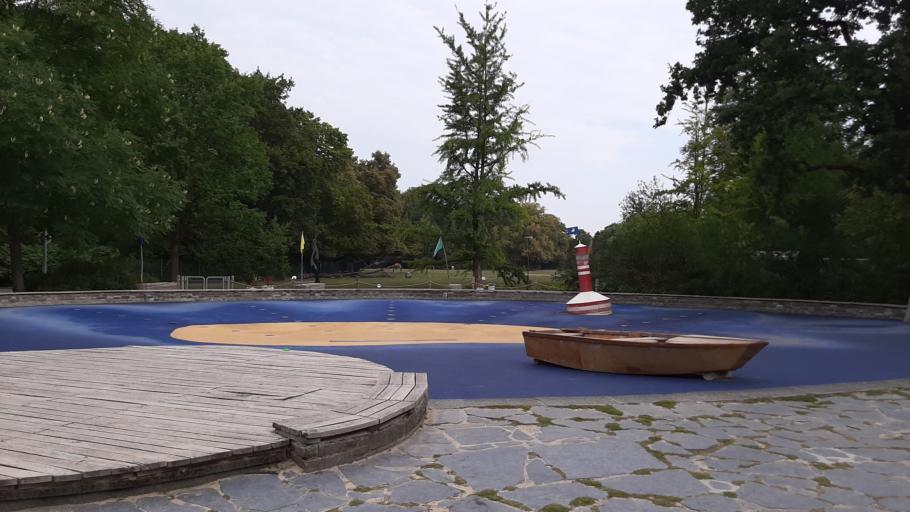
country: DE
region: Berlin
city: Karlshorst
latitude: 52.4997
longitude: 13.5299
